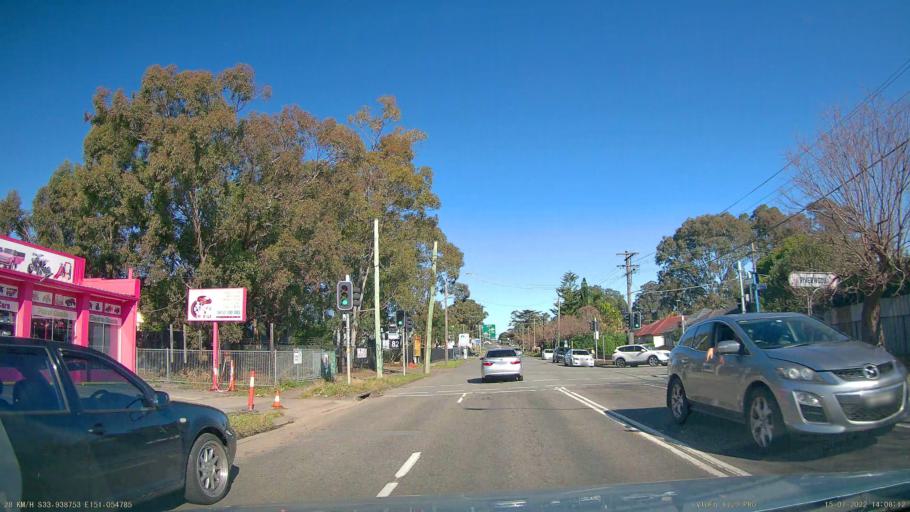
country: AU
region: New South Wales
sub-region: Canterbury
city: Roselands
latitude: -33.9389
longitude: 151.0548
